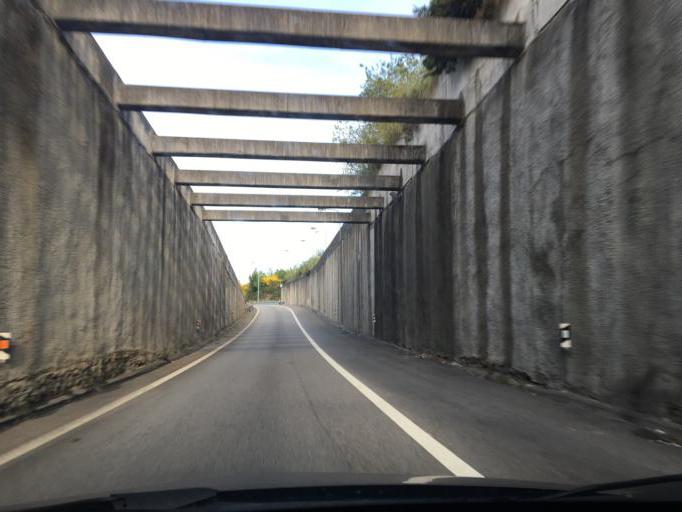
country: PT
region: Porto
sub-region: Maia
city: Maia
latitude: 41.2420
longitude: -8.6286
